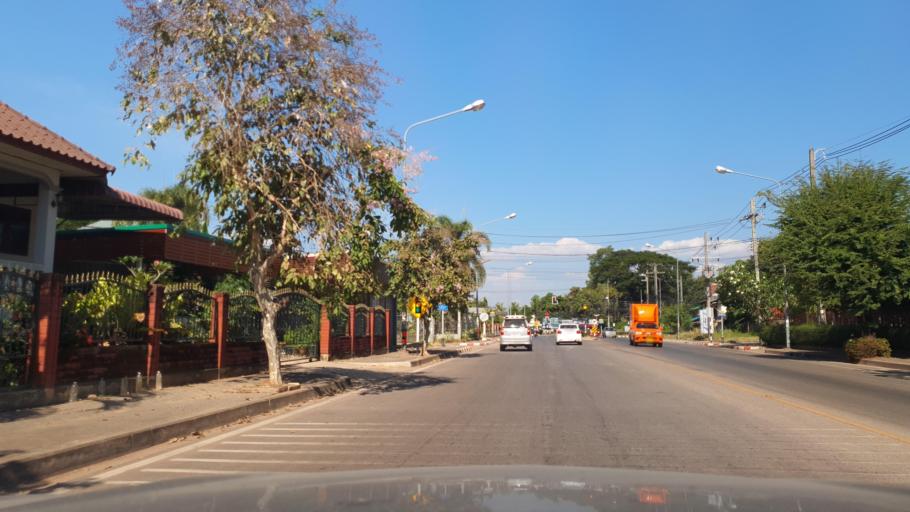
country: TH
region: Sakon Nakhon
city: Sakon Nakhon
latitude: 17.1604
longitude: 104.1270
